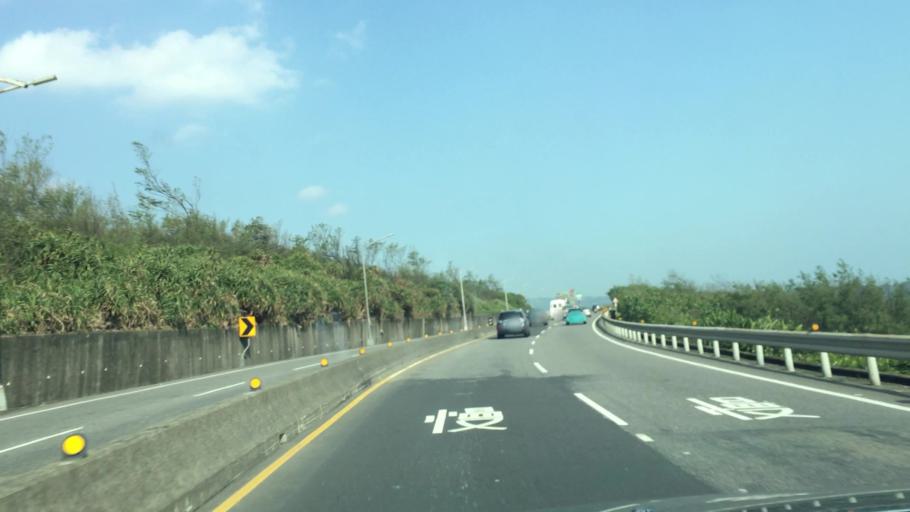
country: TW
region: Taiwan
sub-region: Keelung
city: Keelung
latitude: 25.2075
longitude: 121.6594
